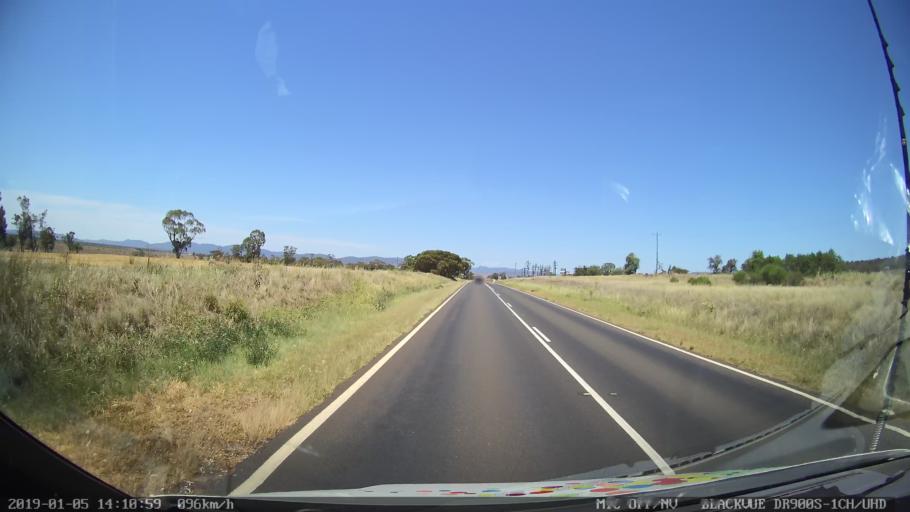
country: AU
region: New South Wales
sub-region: Gunnedah
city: Gunnedah
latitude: -31.2445
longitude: 150.4516
